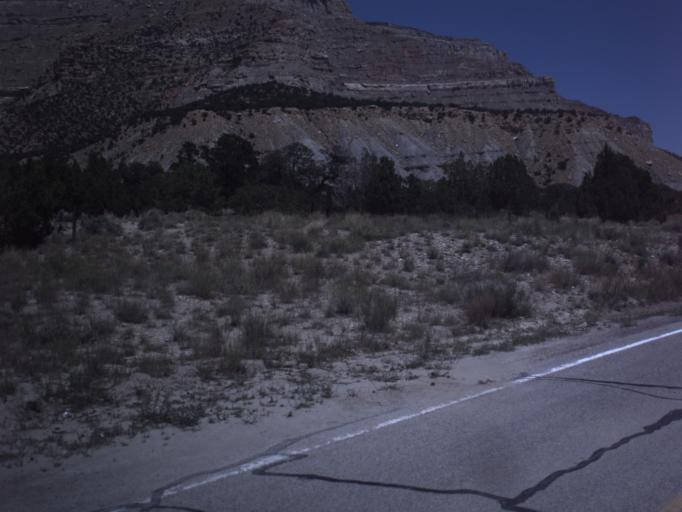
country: US
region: Utah
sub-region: Emery County
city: Orangeville
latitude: 39.2766
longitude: -111.1777
